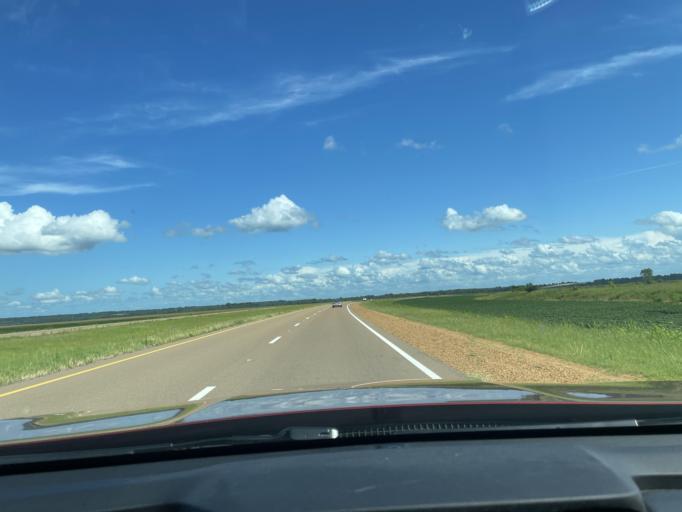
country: US
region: Mississippi
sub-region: Yazoo County
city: Yazoo City
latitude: 32.9497
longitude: -90.4201
